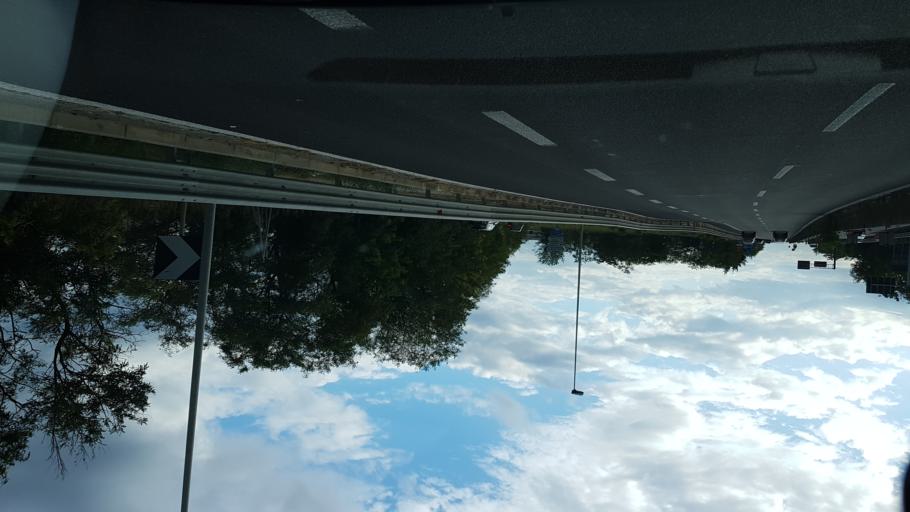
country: IT
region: Apulia
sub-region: Provincia di Brindisi
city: La Rosa
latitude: 40.6173
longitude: 17.9548
